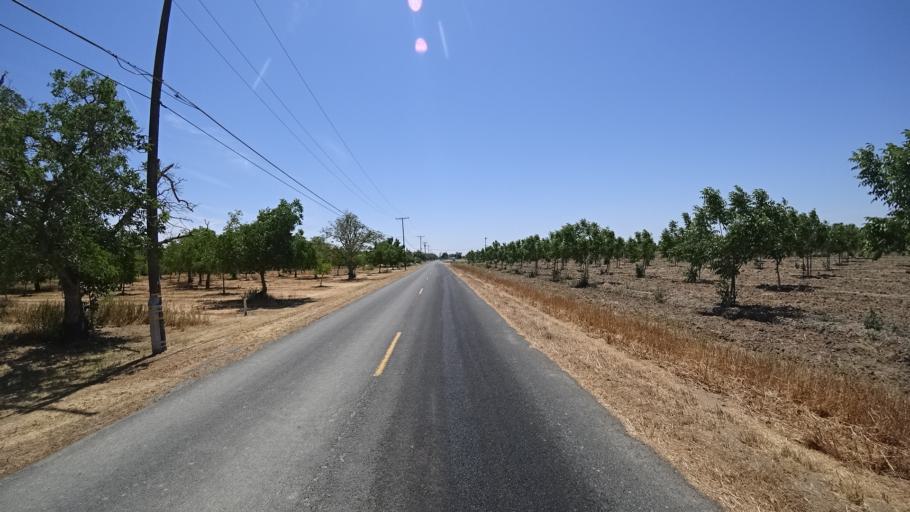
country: US
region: California
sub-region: Kings County
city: Armona
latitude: 36.3222
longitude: -119.7180
